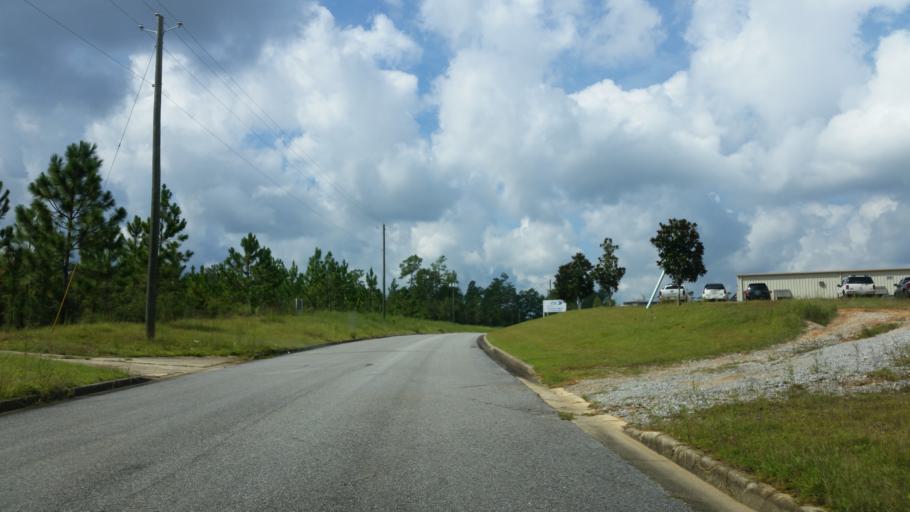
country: US
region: Florida
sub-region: Escambia County
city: Cantonment
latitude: 30.6417
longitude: -87.3476
